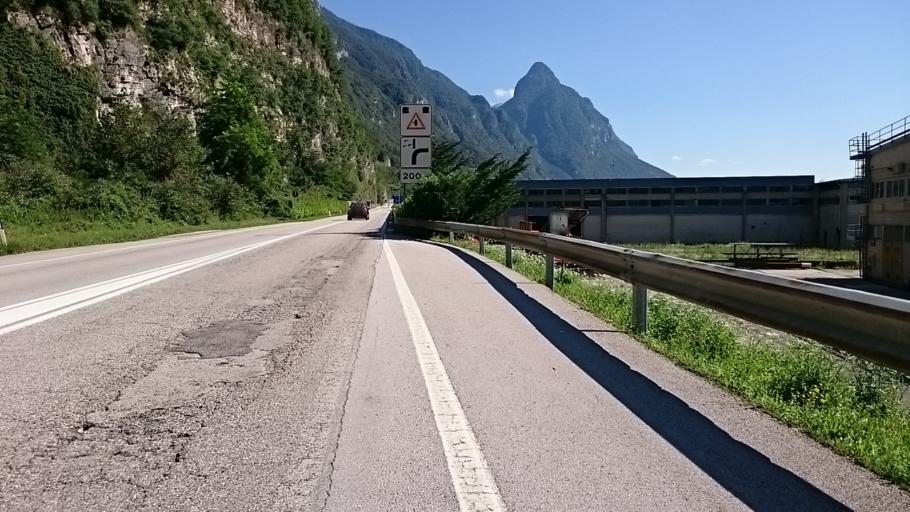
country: IT
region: Veneto
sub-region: Provincia di Belluno
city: Longarone
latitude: 46.2703
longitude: 12.3095
